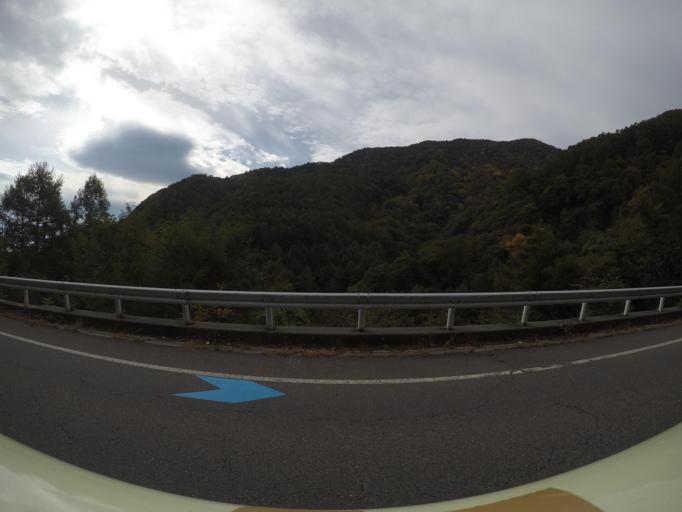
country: JP
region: Nagano
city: Ina
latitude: 35.8772
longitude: 137.8763
